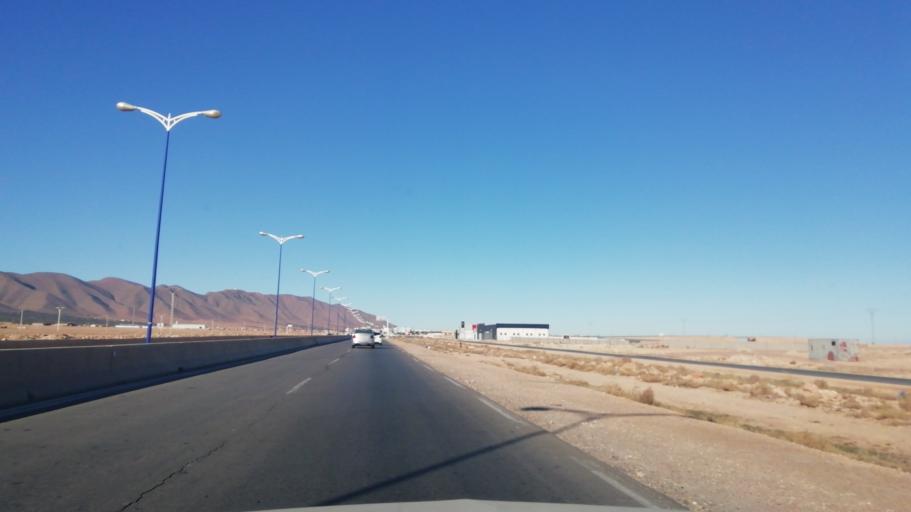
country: DZ
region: Wilaya de Naama
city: Naama
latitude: 33.5051
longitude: -0.2875
